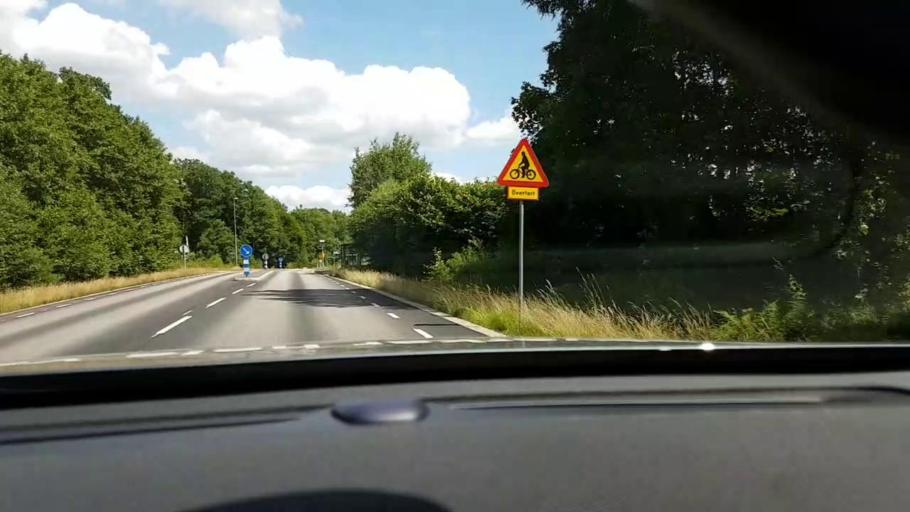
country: SE
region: Skane
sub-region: Hassleholms Kommun
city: Hassleholm
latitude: 56.1672
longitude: 13.7369
